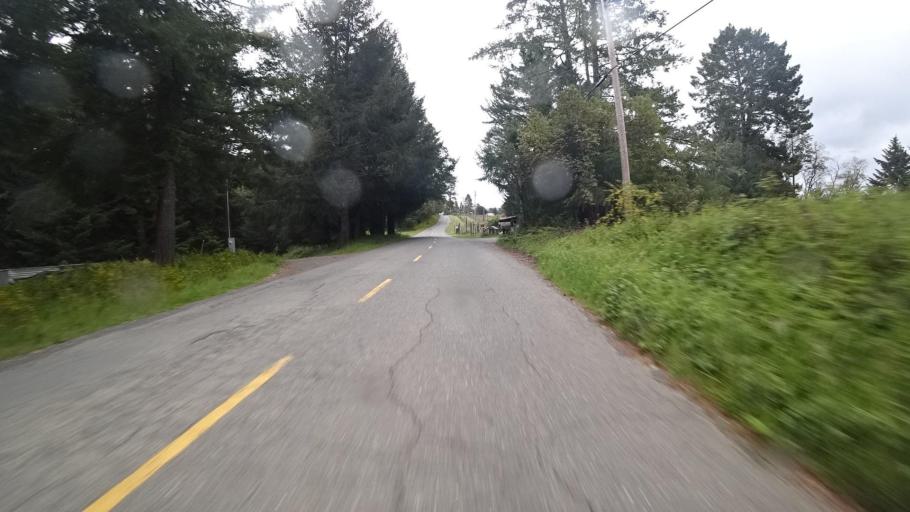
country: US
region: California
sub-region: Humboldt County
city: Redway
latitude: 40.2925
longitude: -123.8161
